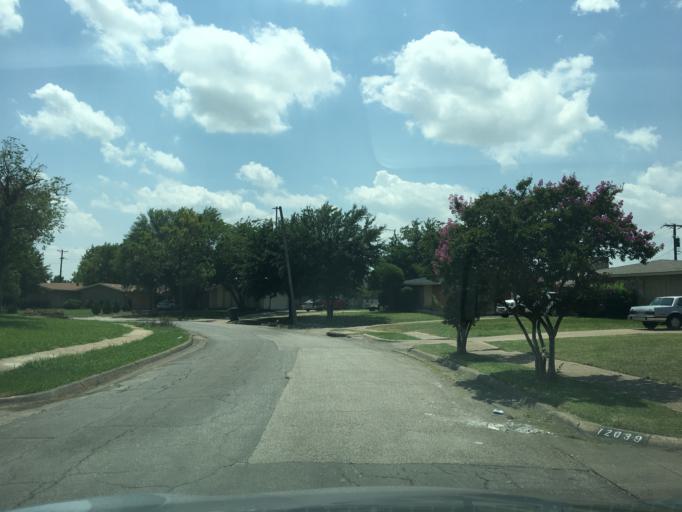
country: US
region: Texas
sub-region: Dallas County
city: Farmers Branch
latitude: 32.9135
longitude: -96.8678
